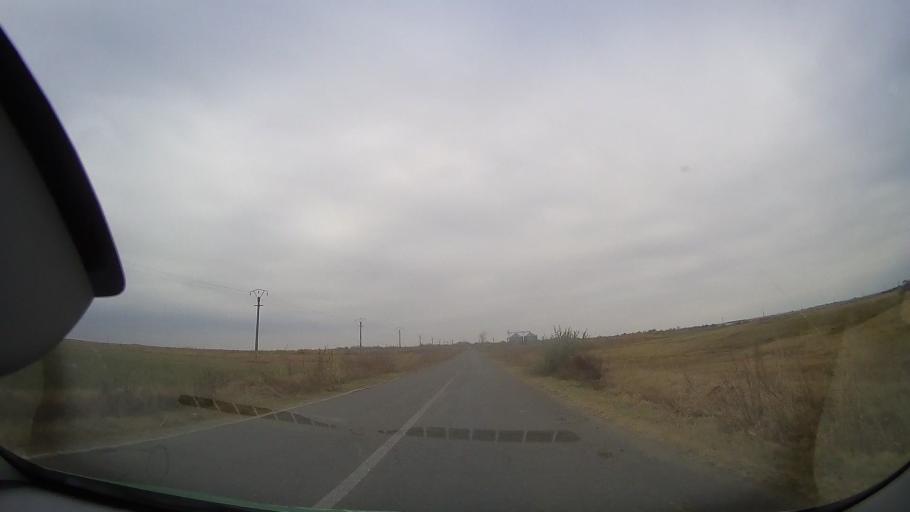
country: RO
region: Buzau
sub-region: Comuna Luciu
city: Luciu
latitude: 44.9666
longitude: 27.1049
